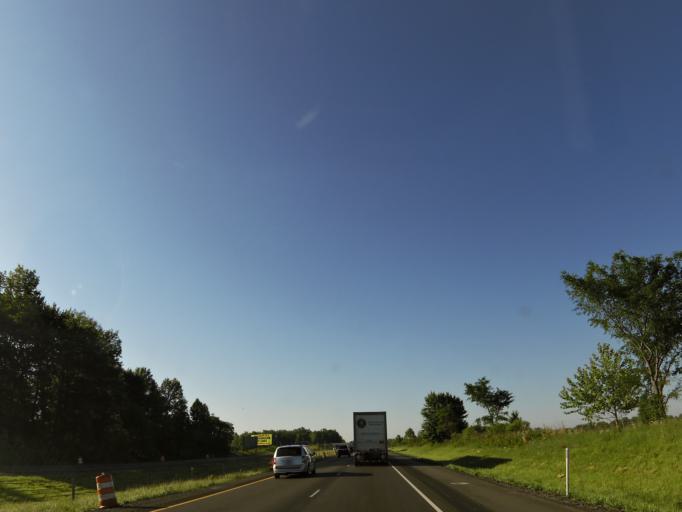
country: US
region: Indiana
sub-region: Jackson County
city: Seymour
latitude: 38.9267
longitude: -85.8389
